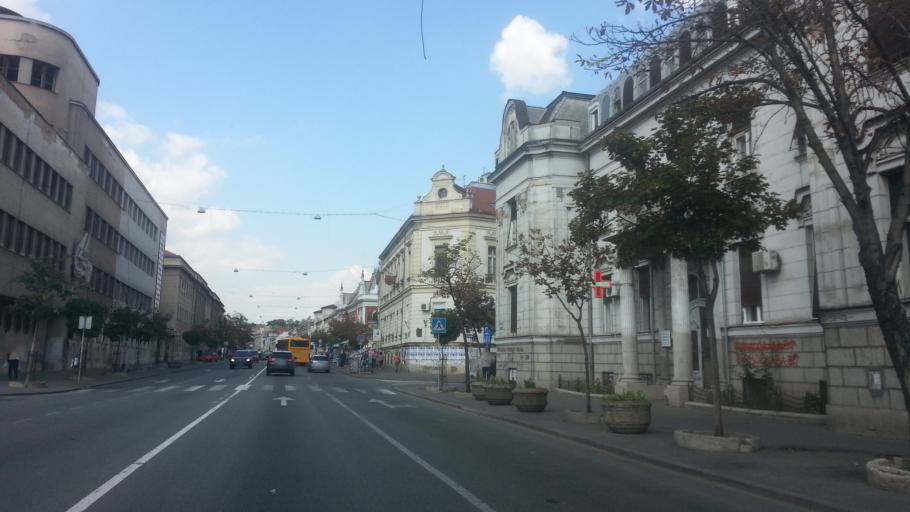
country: RS
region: Central Serbia
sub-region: Belgrade
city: Zemun
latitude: 44.8413
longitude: 20.4140
